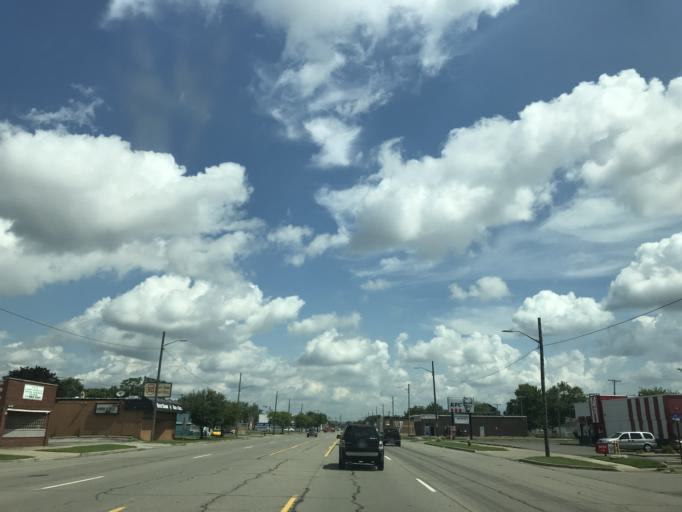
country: US
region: Michigan
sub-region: Wayne County
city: Lincoln Park
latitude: 42.2638
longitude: -83.1859
